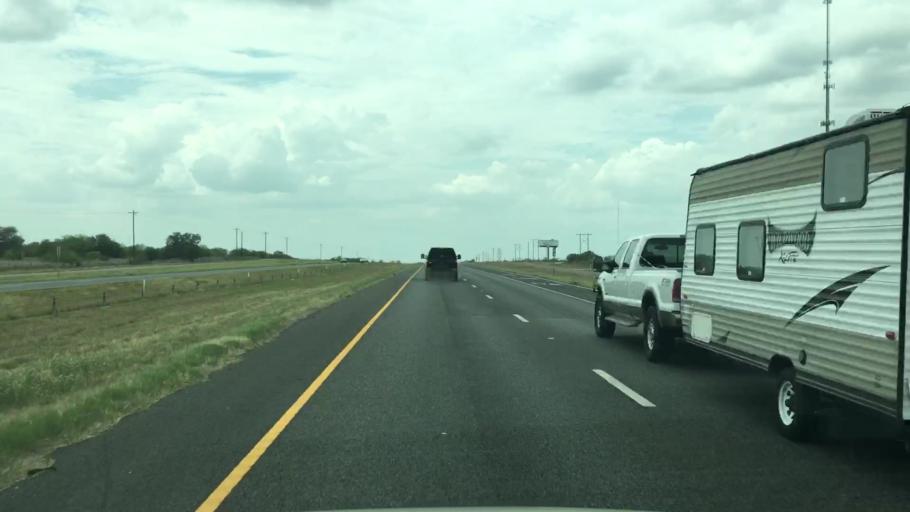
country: US
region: Texas
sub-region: Atascosa County
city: Pleasanton
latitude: 28.7944
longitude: -98.3356
